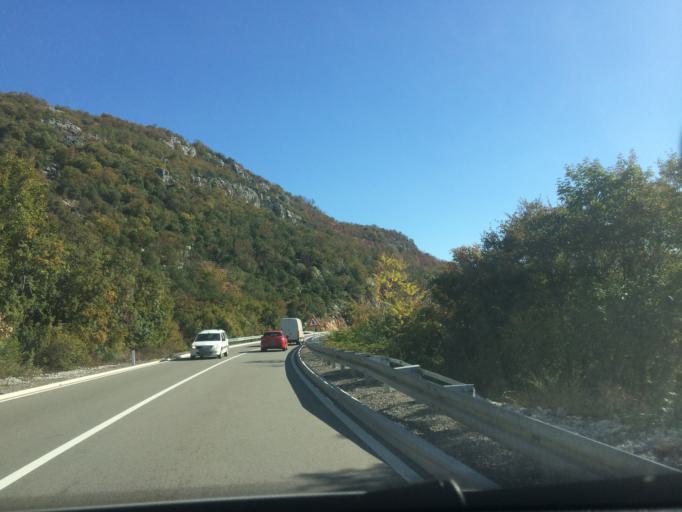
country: ME
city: Mojanovici
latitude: 42.3857
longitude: 19.0884
